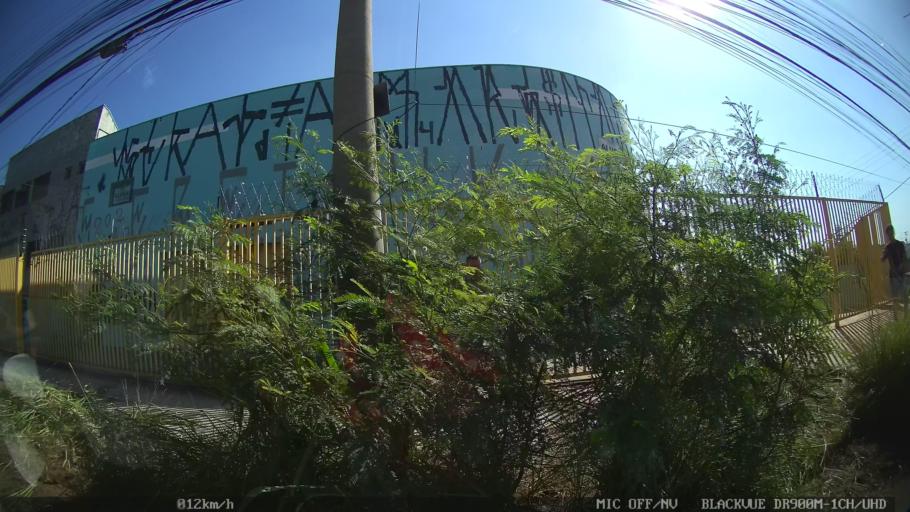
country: BR
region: Sao Paulo
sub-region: Campinas
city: Campinas
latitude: -22.9545
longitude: -47.0939
